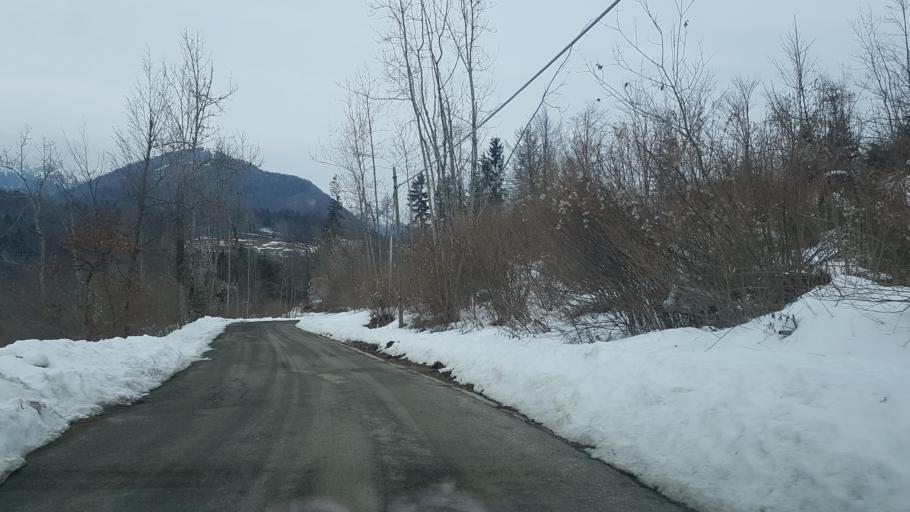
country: IT
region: Friuli Venezia Giulia
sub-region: Provincia di Udine
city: Lauco
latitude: 46.4275
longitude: 12.9423
